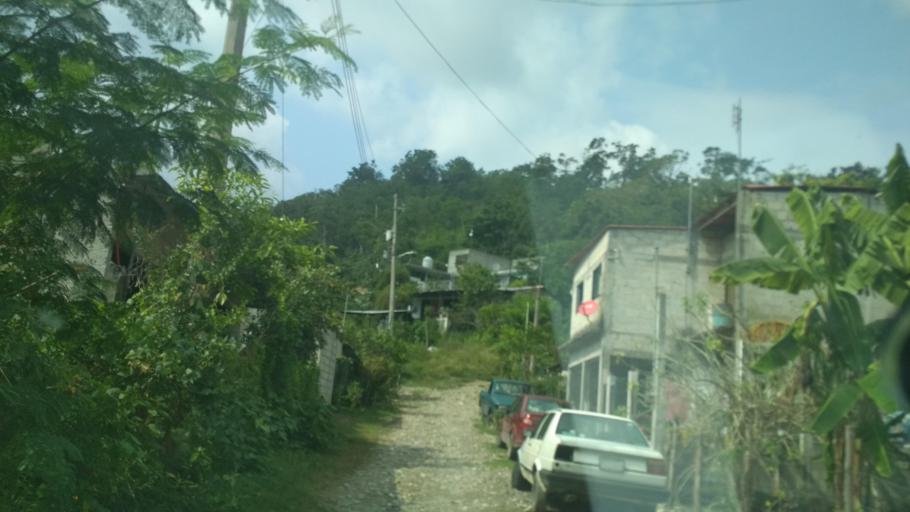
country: MX
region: Veracruz
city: Papantla de Olarte
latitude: 20.4796
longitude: -97.3572
